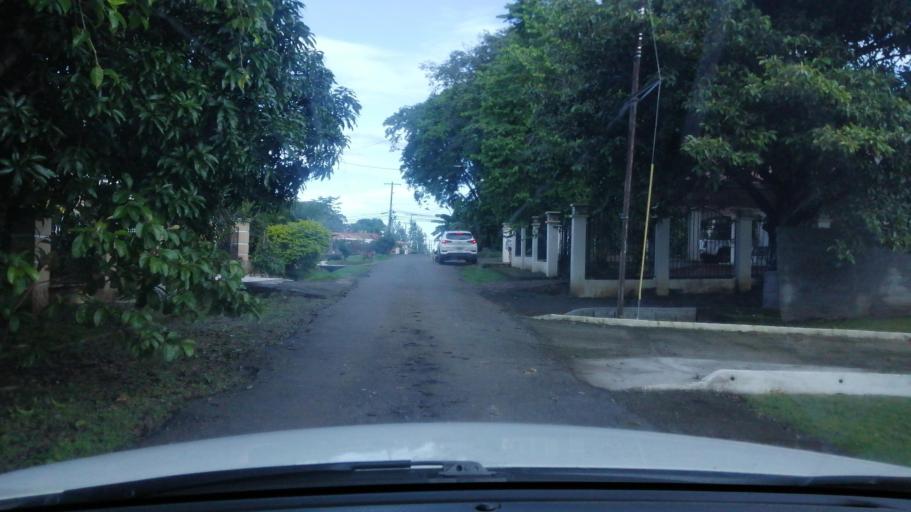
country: PA
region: Chiriqui
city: Mata del Nance
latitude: 8.4562
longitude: -82.4182
